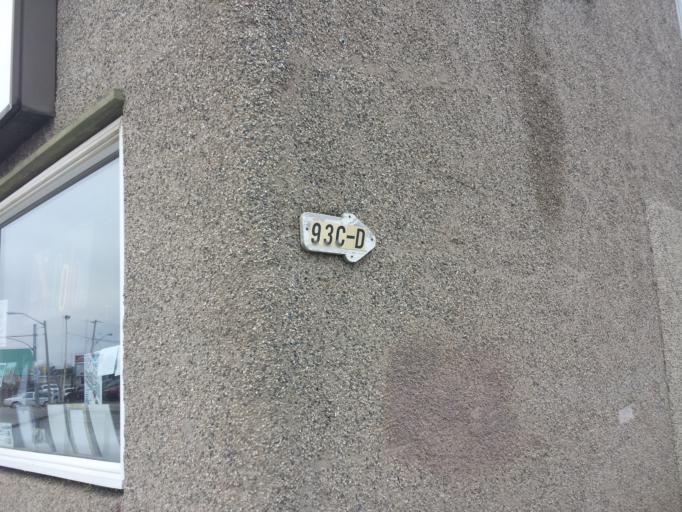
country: CA
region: Ontario
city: Bancroft
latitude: 45.0593
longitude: -77.8547
